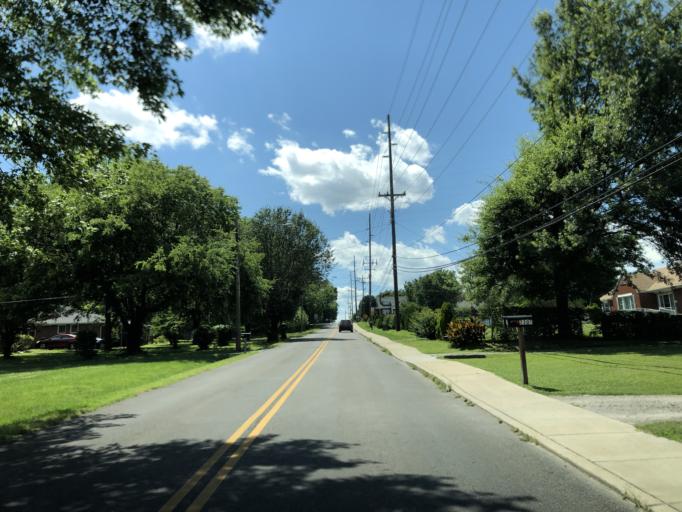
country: US
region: Tennessee
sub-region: Davidson County
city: Nashville
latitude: 36.1816
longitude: -86.7238
